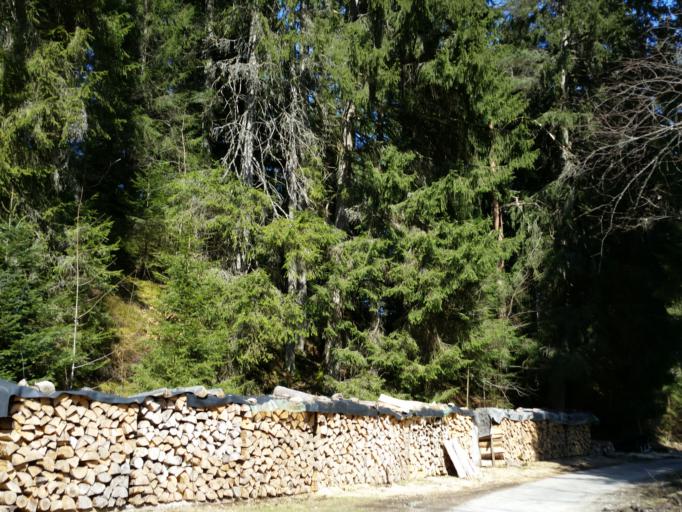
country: DE
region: Baden-Wuerttemberg
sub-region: Karlsruhe Region
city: Freudenstadt
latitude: 48.4654
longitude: 8.3986
